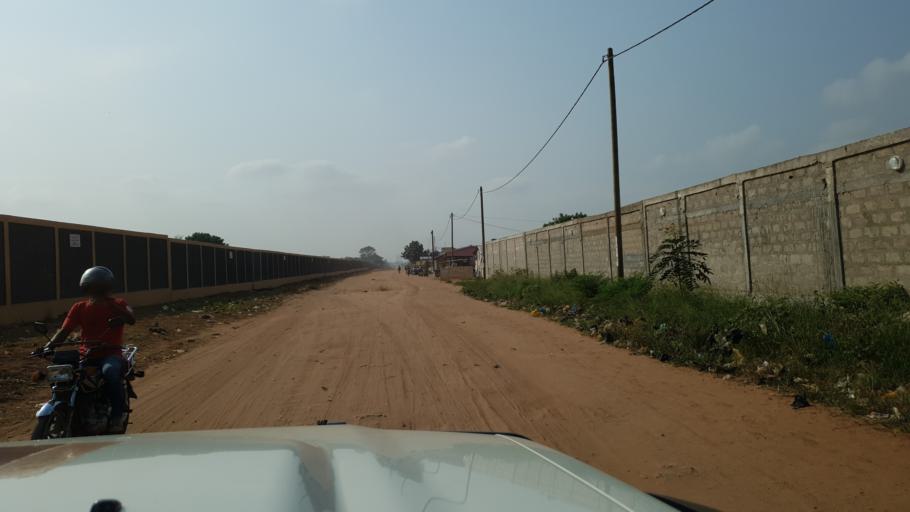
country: TG
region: Maritime
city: Lome
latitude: 6.1807
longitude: 1.2088
